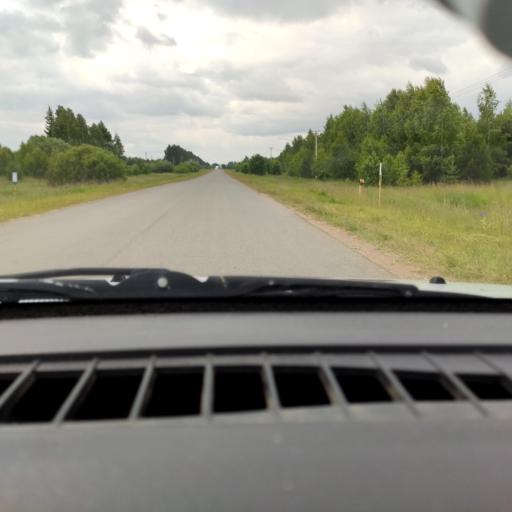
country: RU
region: Perm
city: Uinskoye
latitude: 57.1125
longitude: 56.6661
